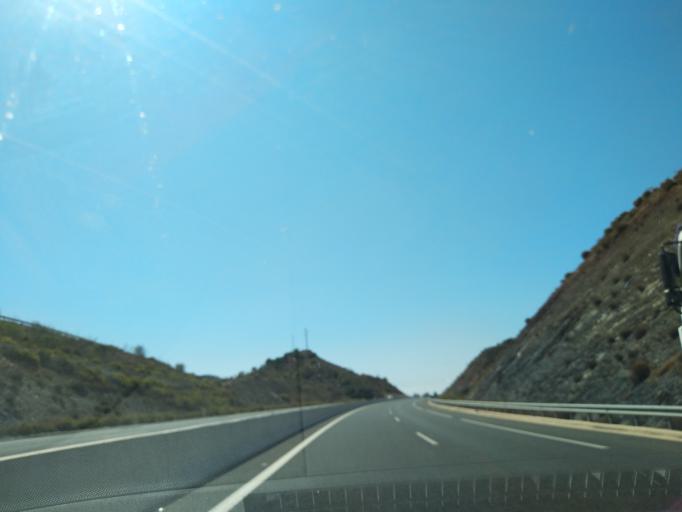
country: ES
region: Andalusia
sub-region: Provincia de Malaga
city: Almogia
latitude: 36.8268
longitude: -4.4696
